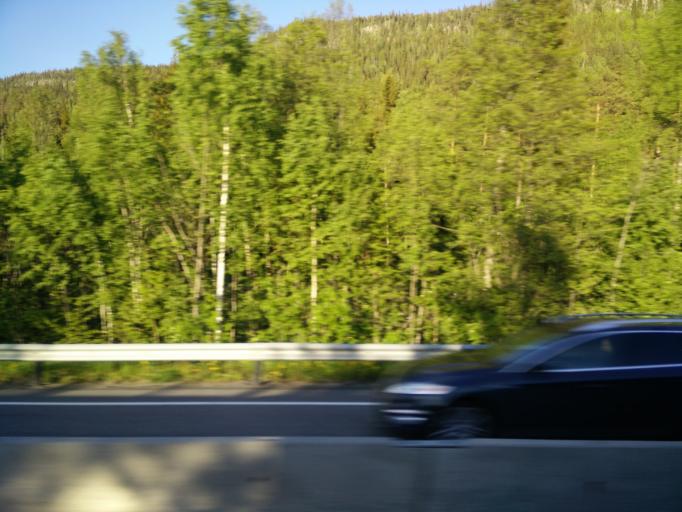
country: NO
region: Buskerud
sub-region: Hole
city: Vik
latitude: 60.0361
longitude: 10.2713
